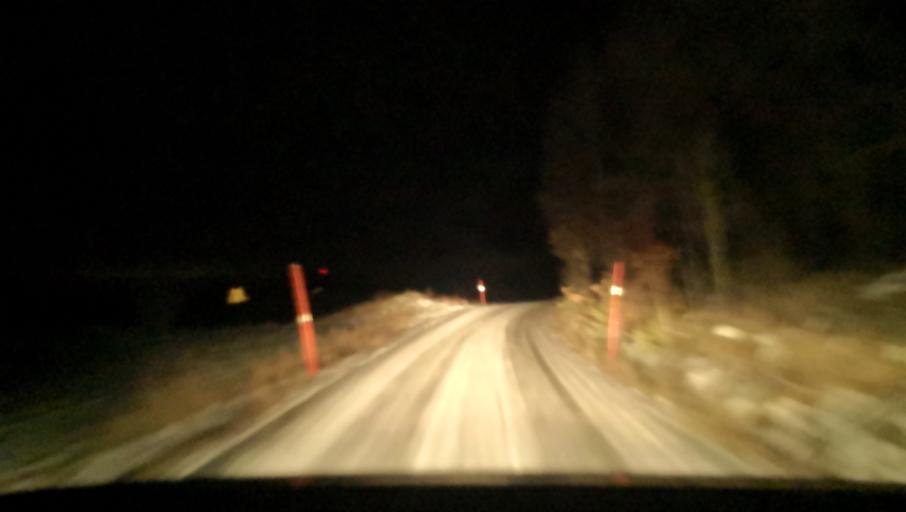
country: SE
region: Uppsala
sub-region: Enkopings Kommun
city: Irsta
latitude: 59.6517
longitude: 16.8655
